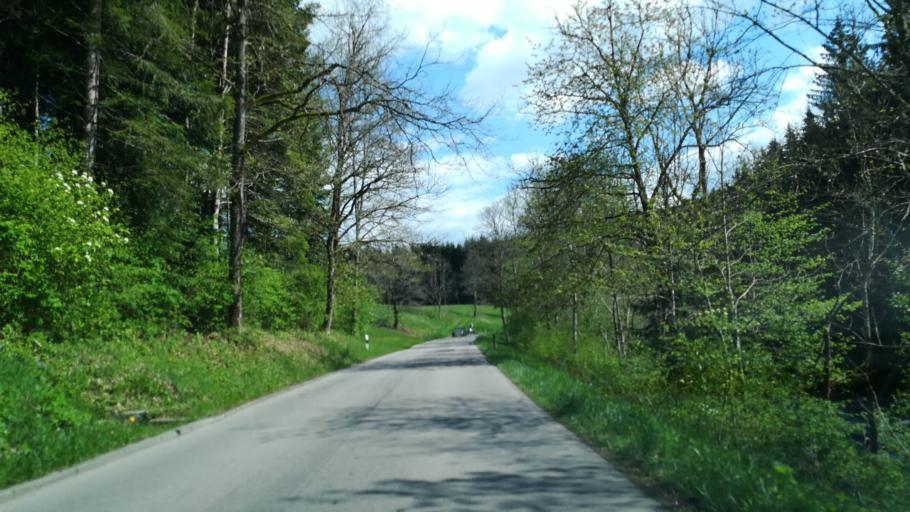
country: DE
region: Baden-Wuerttemberg
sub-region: Freiburg Region
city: Blumberg
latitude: 47.8478
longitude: 8.4587
